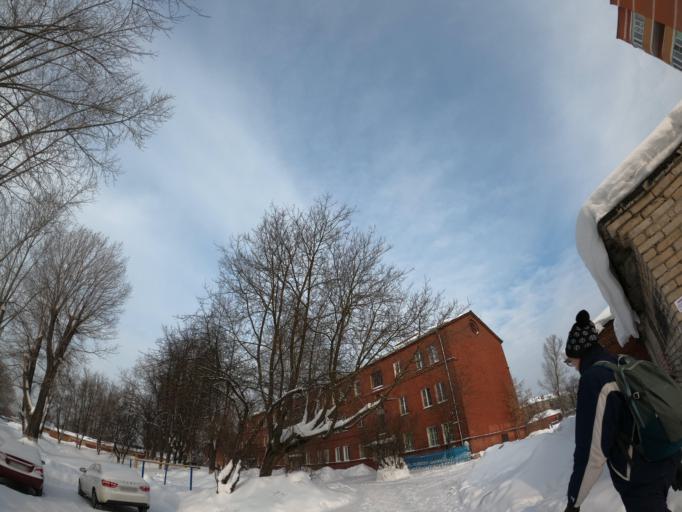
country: RU
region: Moskovskaya
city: Elektrogorsk
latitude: 55.8885
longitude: 38.7731
